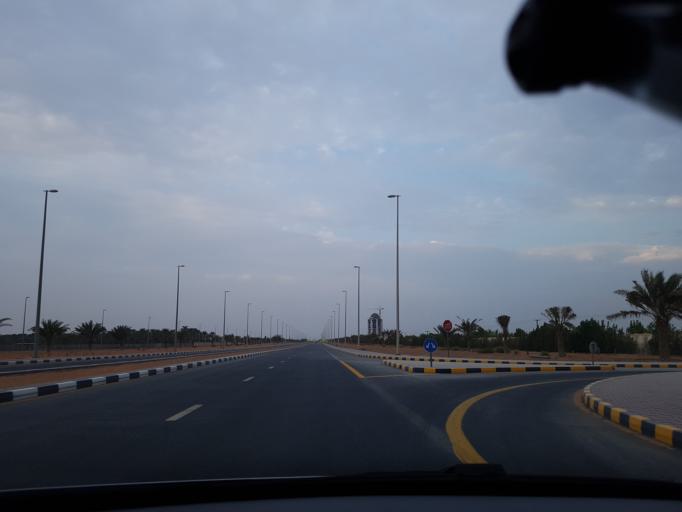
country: AE
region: Ash Shariqah
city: Adh Dhayd
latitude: 25.2760
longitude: 55.9127
